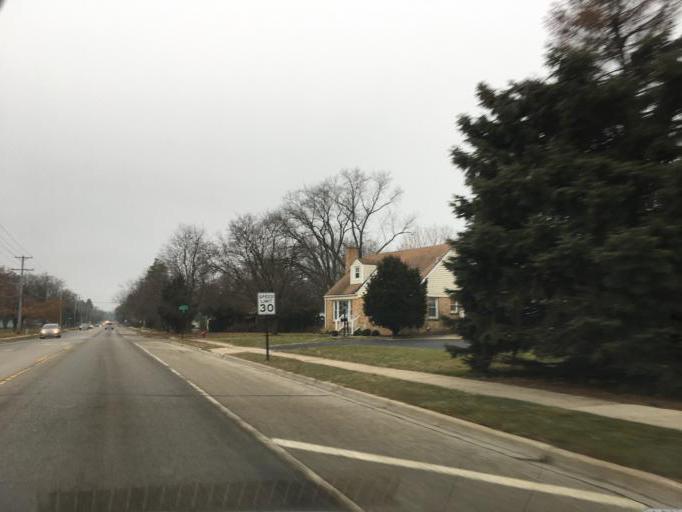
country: US
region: Illinois
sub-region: McHenry County
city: Lakewood
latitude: 42.2282
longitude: -88.3364
